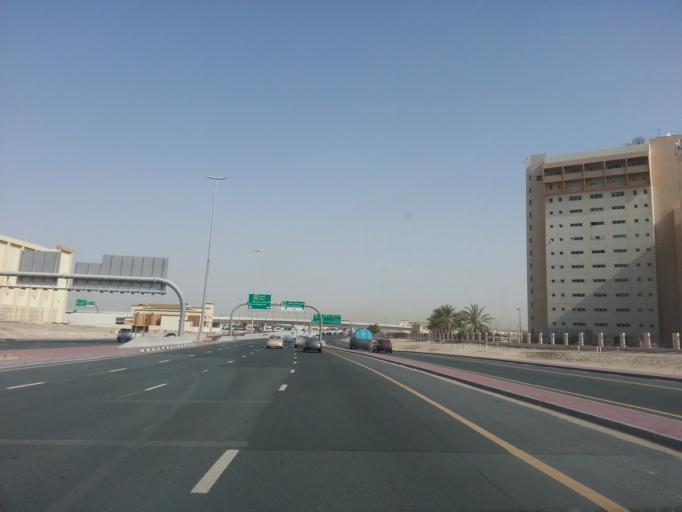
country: AE
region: Dubai
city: Dubai
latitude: 25.0609
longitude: 55.1363
